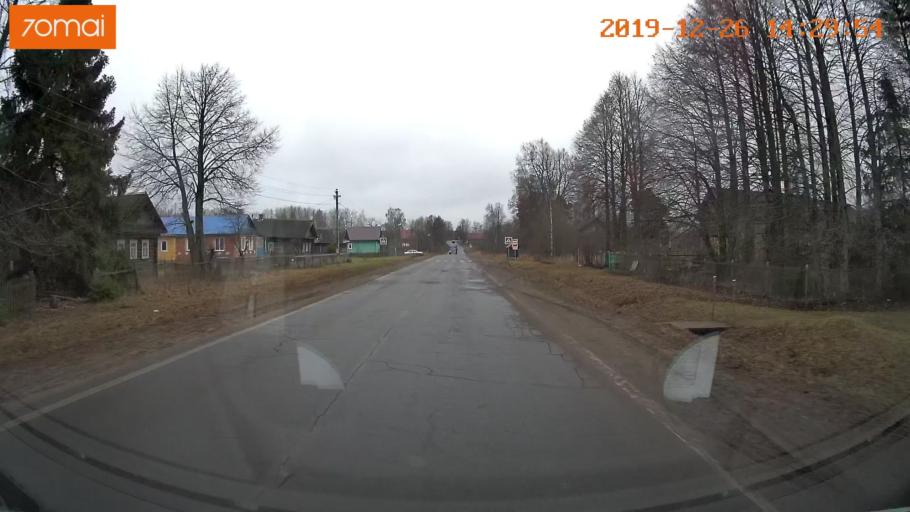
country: RU
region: Jaroslavl
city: Poshekhon'ye
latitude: 58.4584
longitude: 39.0400
